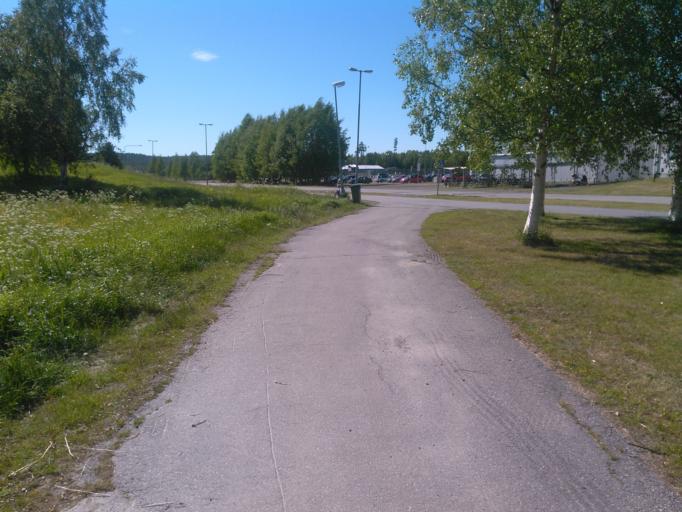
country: SE
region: Vaesterbotten
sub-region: Umea Kommun
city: Roback
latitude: 63.8198
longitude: 20.2050
